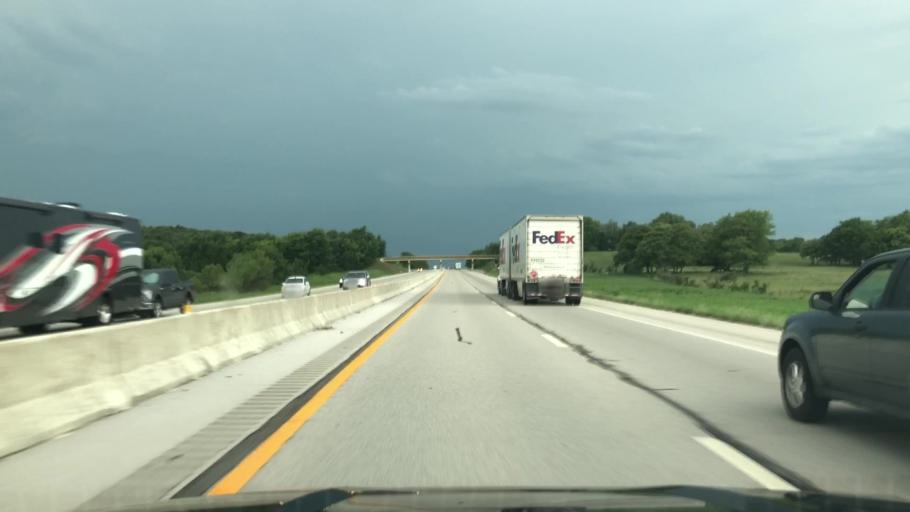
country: US
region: Oklahoma
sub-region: Rogers County
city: Justice
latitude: 36.3434
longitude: -95.4855
